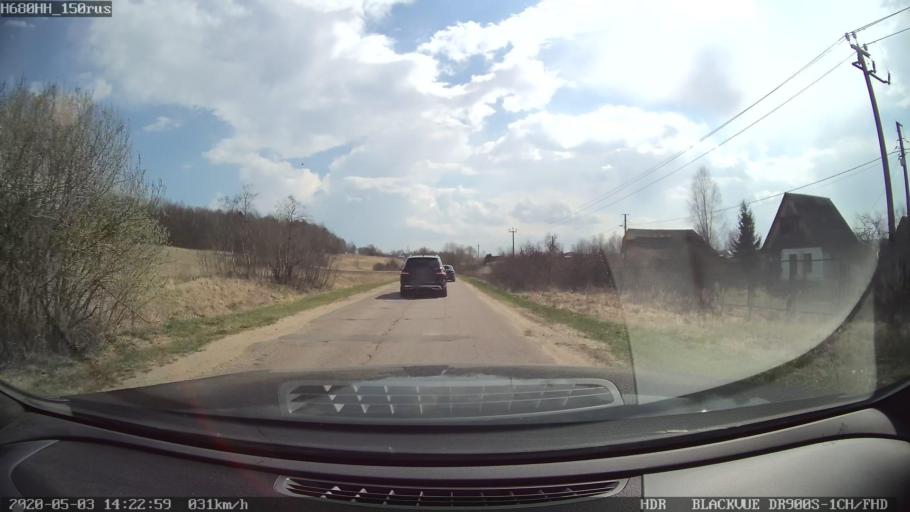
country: RU
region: Moskovskaya
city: Solnechnogorsk
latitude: 56.2556
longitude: 36.9916
